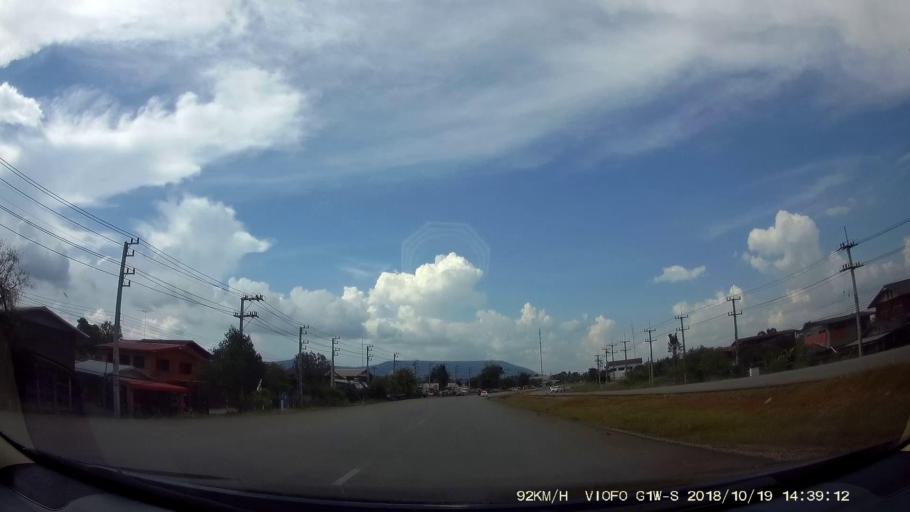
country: TH
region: Chaiyaphum
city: Kaeng Khro
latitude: 16.2234
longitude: 102.1965
